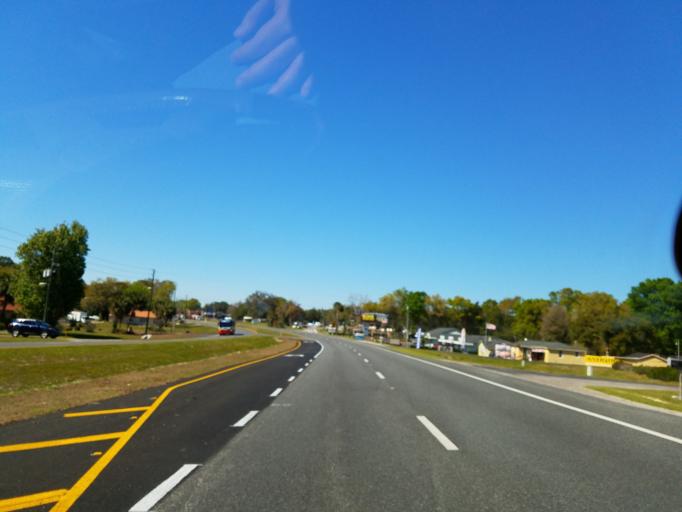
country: US
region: Florida
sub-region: Marion County
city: Belleview
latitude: 29.0543
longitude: -82.0469
